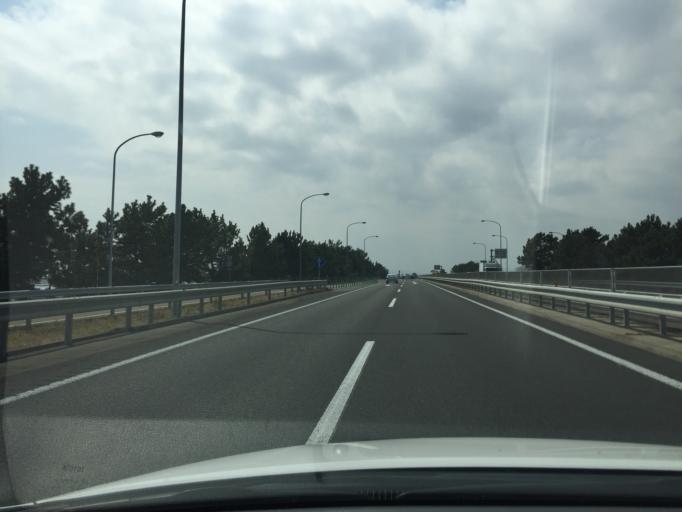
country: JP
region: Miyagi
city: Sendai
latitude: 38.1819
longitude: 140.9316
